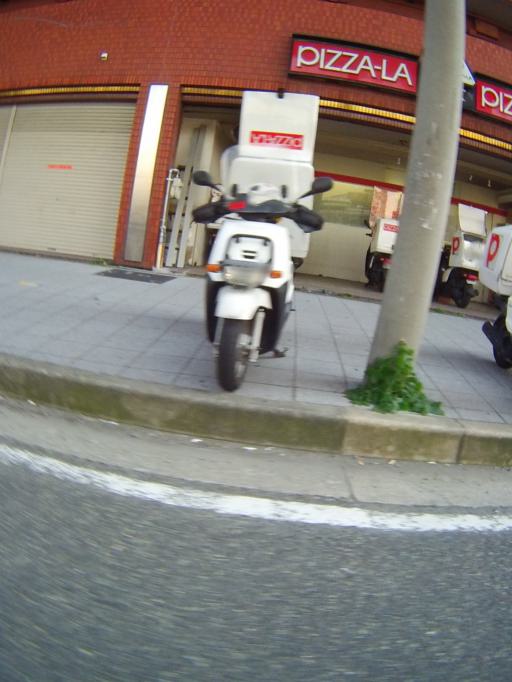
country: JP
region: Osaka
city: Osaka-shi
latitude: 34.6570
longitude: 135.4712
